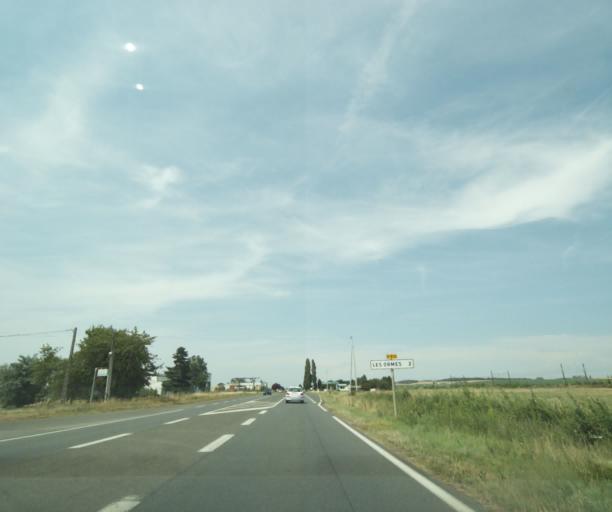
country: FR
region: Poitou-Charentes
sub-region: Departement de la Vienne
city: Dange-Saint-Romain
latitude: 46.9458
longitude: 0.6074
